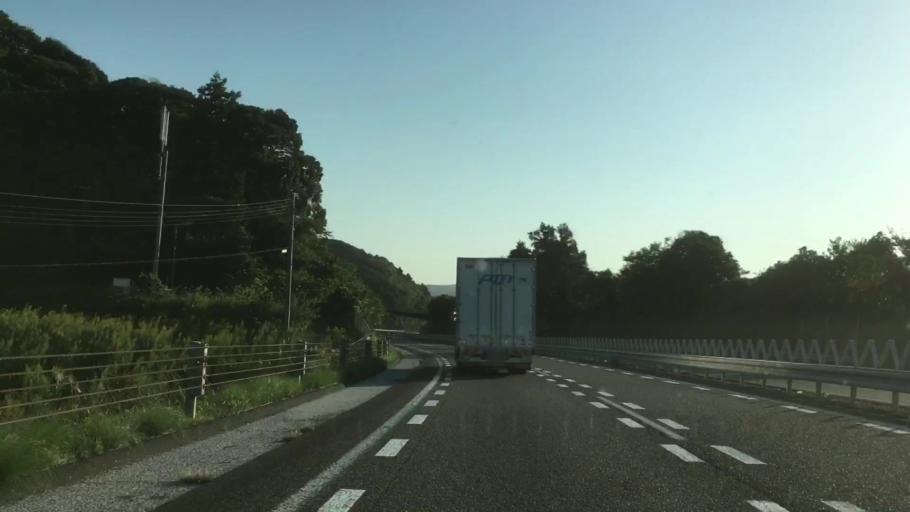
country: JP
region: Yamaguchi
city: Onoda
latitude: 34.1442
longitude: 131.2312
